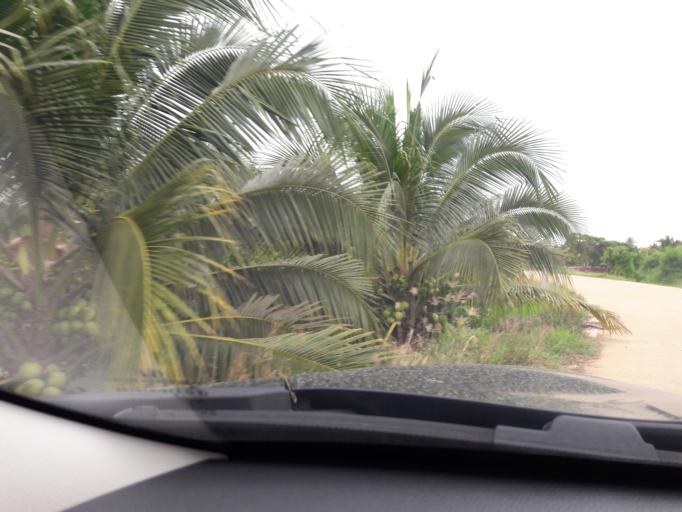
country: TH
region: Ratchaburi
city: Damnoen Saduak
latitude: 13.6076
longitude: 99.9686
